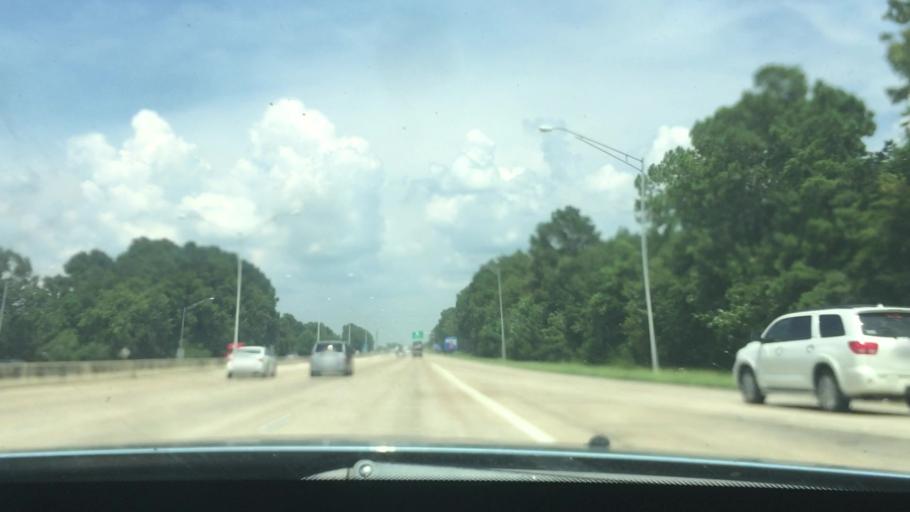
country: US
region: Louisiana
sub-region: East Baton Rouge Parish
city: Shenandoah
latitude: 30.4389
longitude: -91.0208
